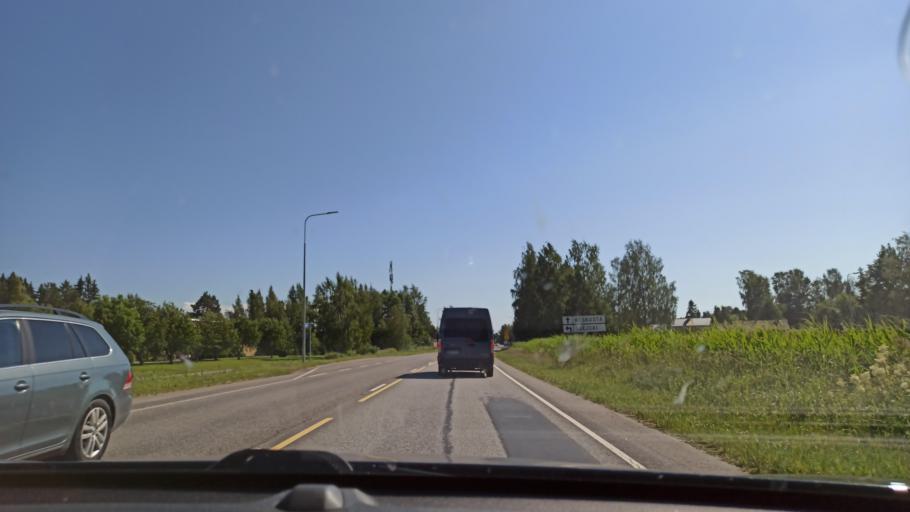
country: FI
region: Satakunta
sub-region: Pori
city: Pori
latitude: 61.5075
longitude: 21.8033
